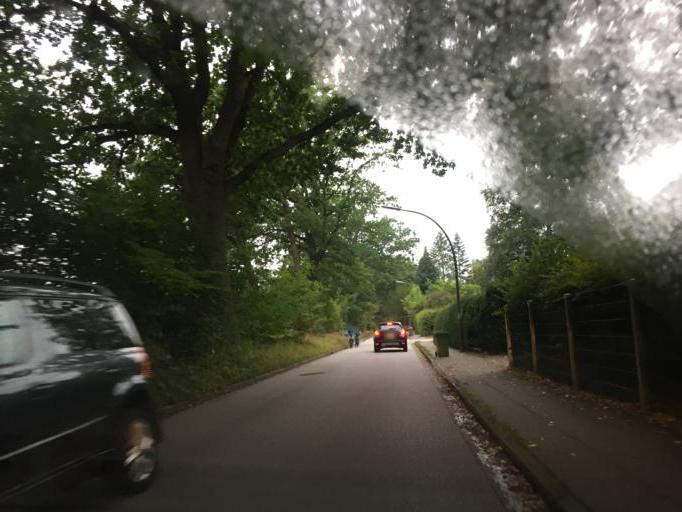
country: DE
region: Hamburg
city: Wellingsbuettel
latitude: 53.6347
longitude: 10.0754
